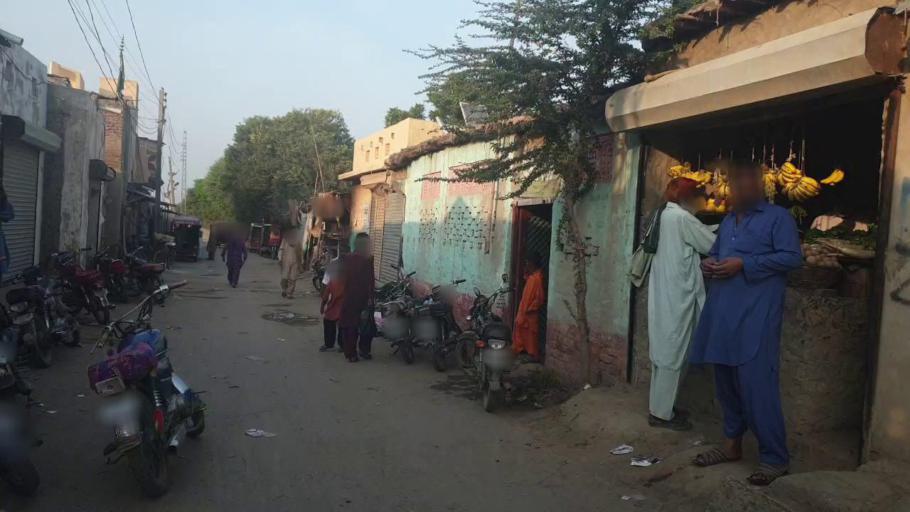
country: PK
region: Sindh
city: Tando Jam
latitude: 25.4447
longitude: 68.5848
